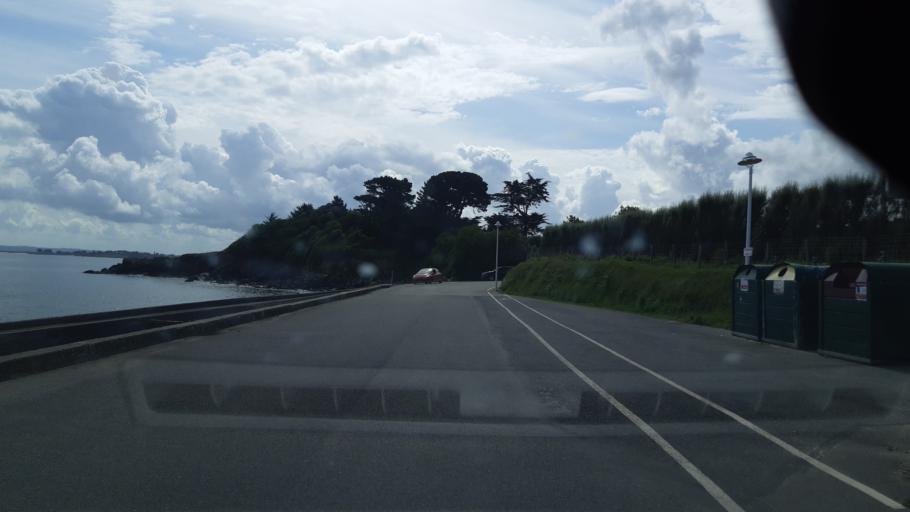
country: FR
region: Brittany
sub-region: Departement du Finistere
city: Saint-Pol-de-Leon
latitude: 48.6933
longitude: -3.9684
